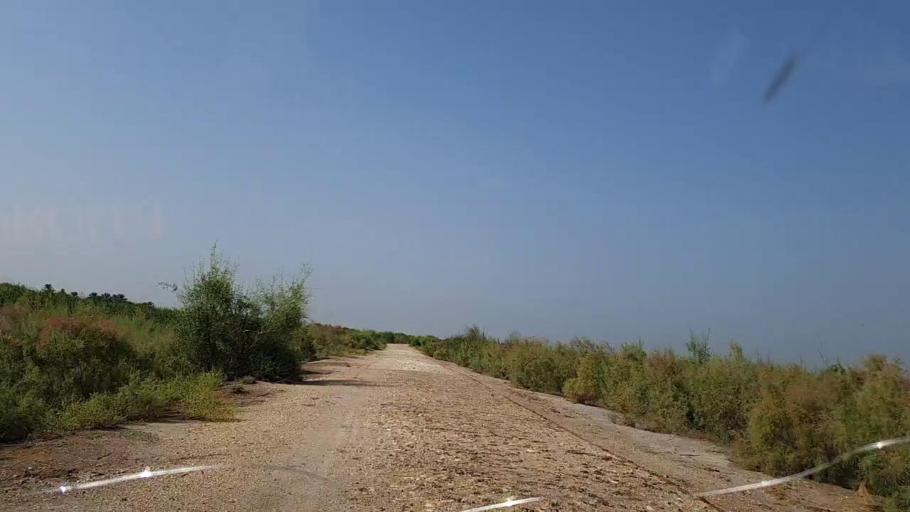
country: PK
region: Sindh
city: Khanpur
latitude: 27.7028
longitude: 69.3859
